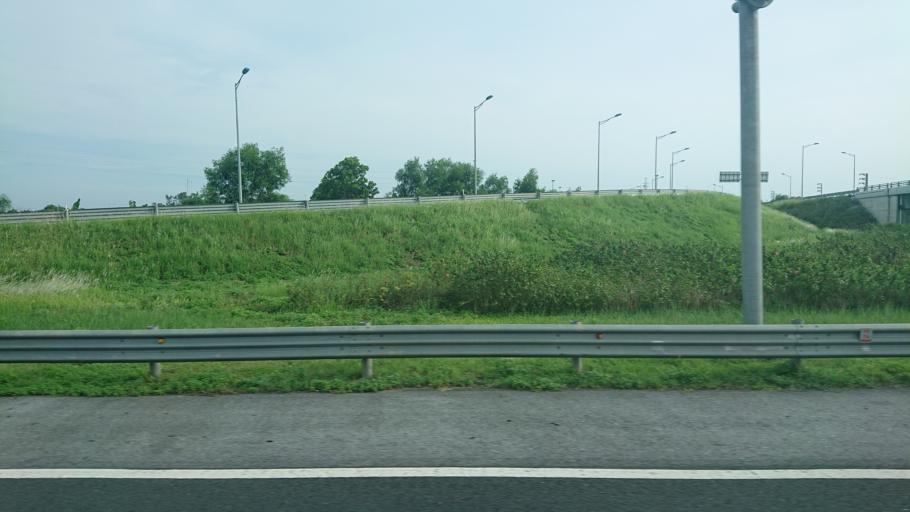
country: VN
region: Hai Phong
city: An Lao
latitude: 20.8030
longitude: 106.5256
